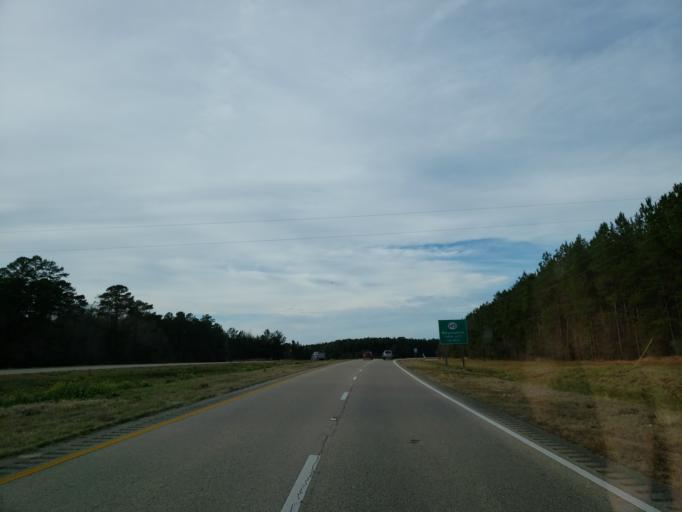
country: US
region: Mississippi
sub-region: Wayne County
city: Waynesboro
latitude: 31.6277
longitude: -88.5891
